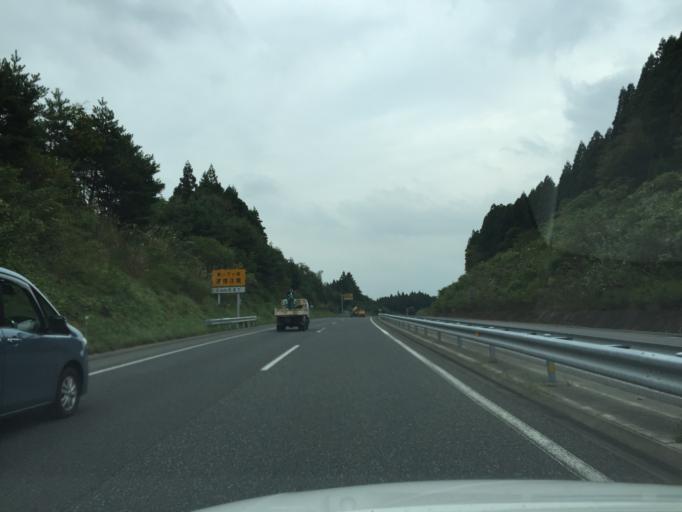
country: JP
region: Fukushima
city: Iwaki
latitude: 37.0940
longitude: 140.7832
